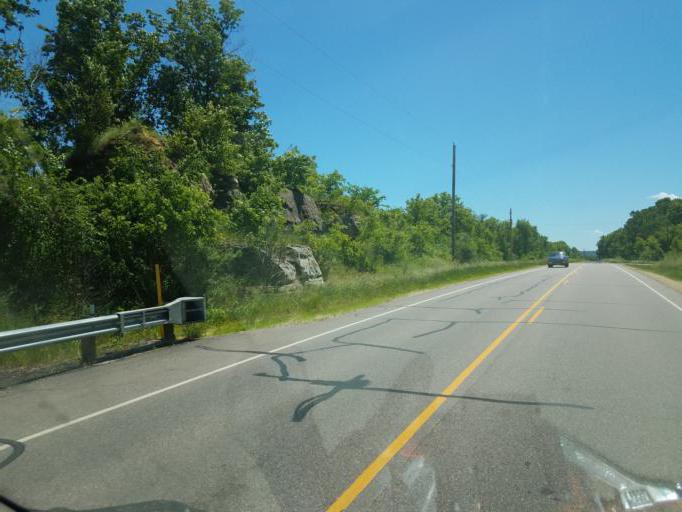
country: US
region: Wisconsin
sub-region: Juneau County
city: Elroy
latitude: 43.7220
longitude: -90.2659
